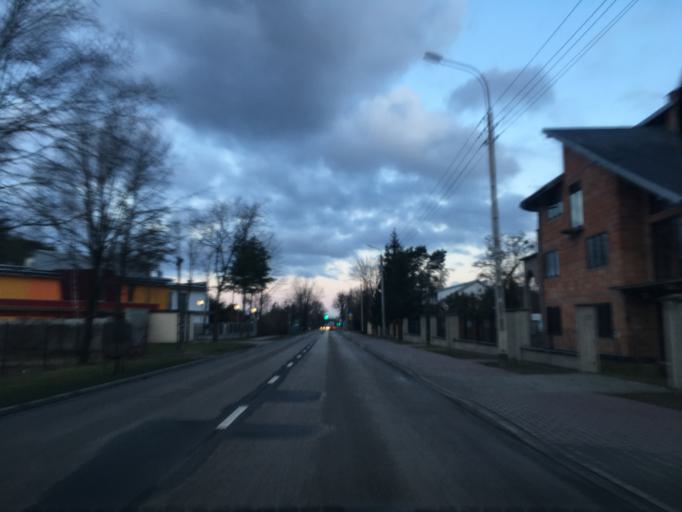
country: PL
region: Masovian Voivodeship
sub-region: Powiat grodziski
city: Grodzisk Mazowiecki
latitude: 52.0987
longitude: 20.6480
